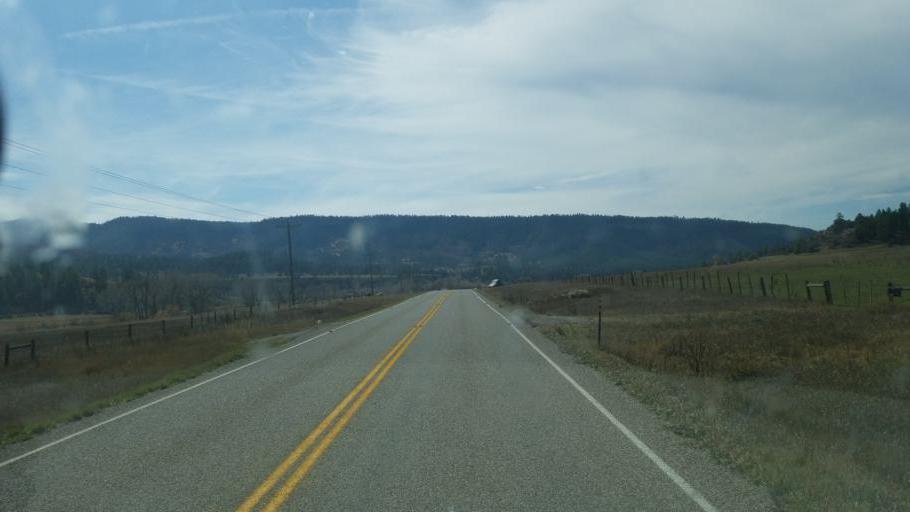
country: US
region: New Mexico
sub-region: Rio Arriba County
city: Dulce
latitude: 37.0444
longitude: -106.8427
